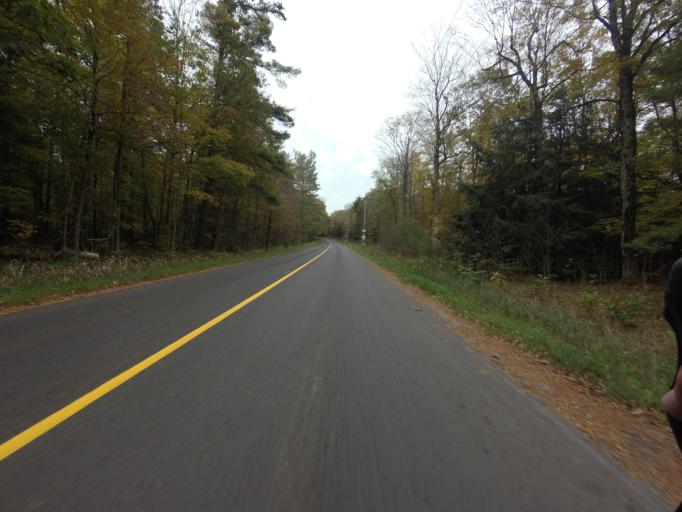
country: CA
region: Ontario
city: Gananoque
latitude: 44.5710
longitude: -76.1097
